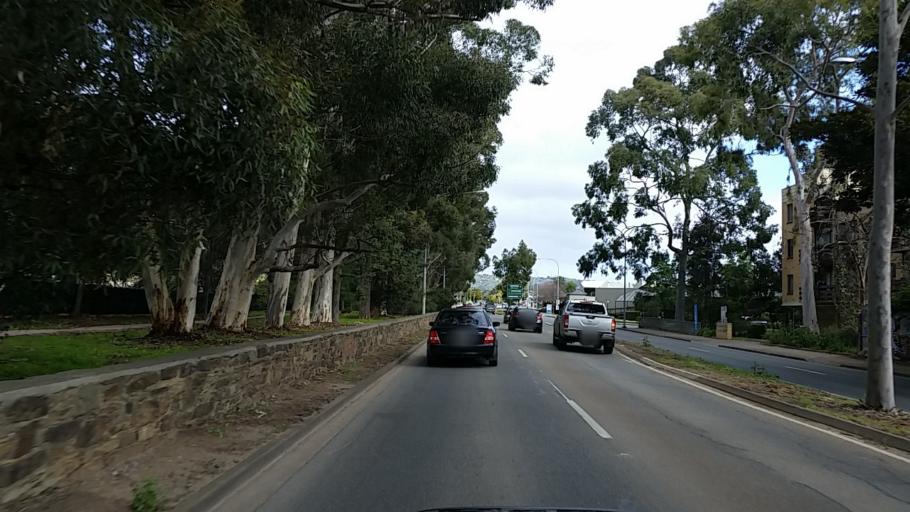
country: AU
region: South Australia
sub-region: Unley
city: Fullarton
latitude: -34.9439
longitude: 138.6249
